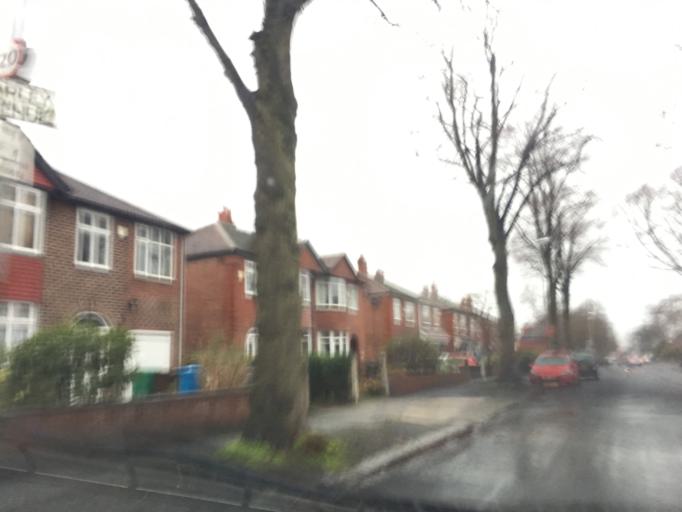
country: GB
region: England
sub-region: Manchester
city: Chorlton cum Hardy
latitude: 53.4252
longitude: -2.2630
